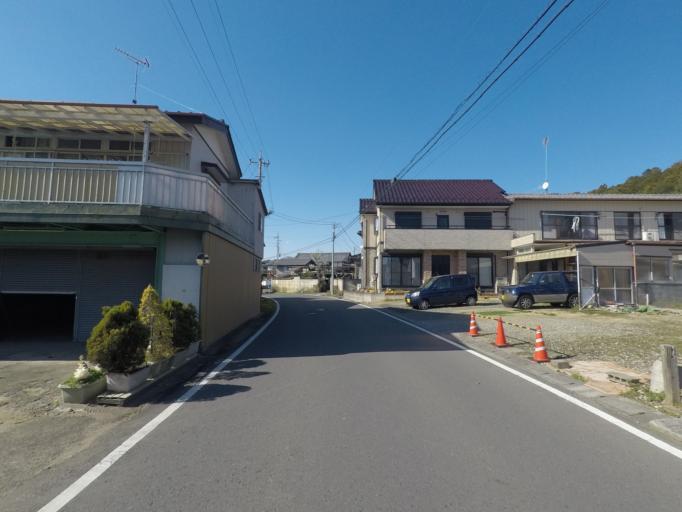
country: JP
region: Ibaraki
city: Tsukuba
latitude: 36.1815
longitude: 140.0828
